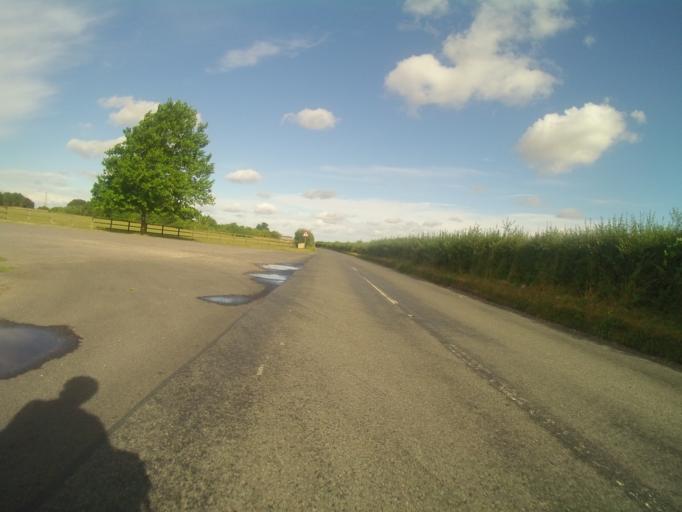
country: GB
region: England
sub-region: Wiltshire
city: Bulford
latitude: 51.1859
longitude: -1.7457
